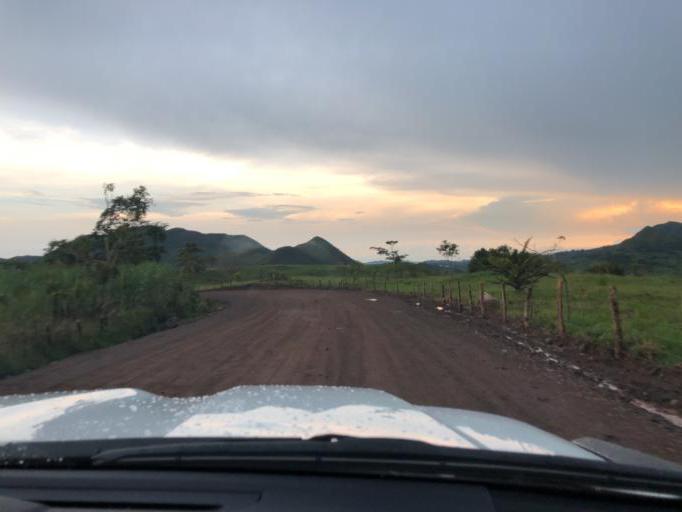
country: NI
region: Chontales
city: La Libertad
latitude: 12.1861
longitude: -85.1745
